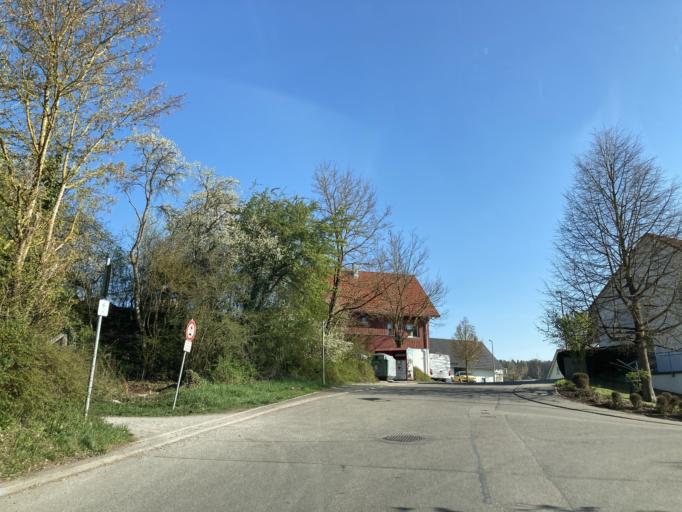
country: DE
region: Baden-Wuerttemberg
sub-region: Regierungsbezirk Stuttgart
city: Hildrizhausen
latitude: 48.5537
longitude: 8.9742
